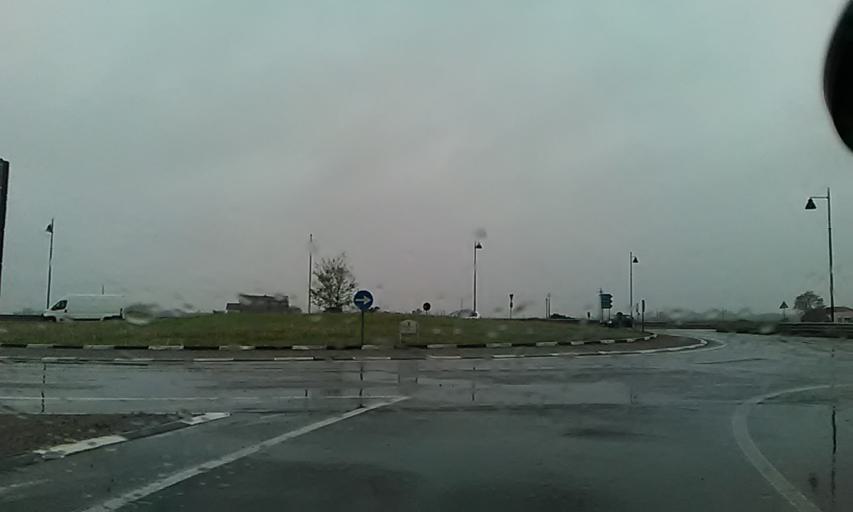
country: IT
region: Piedmont
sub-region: Provincia di Vercelli
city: Formigliana
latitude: 45.4266
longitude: 8.2977
